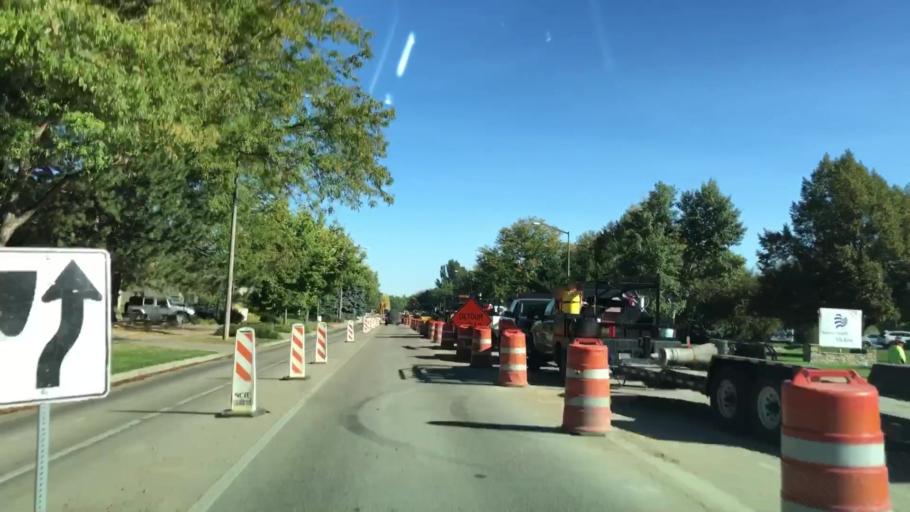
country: US
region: Colorado
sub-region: Larimer County
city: Loveland
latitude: 40.4128
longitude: -105.0537
